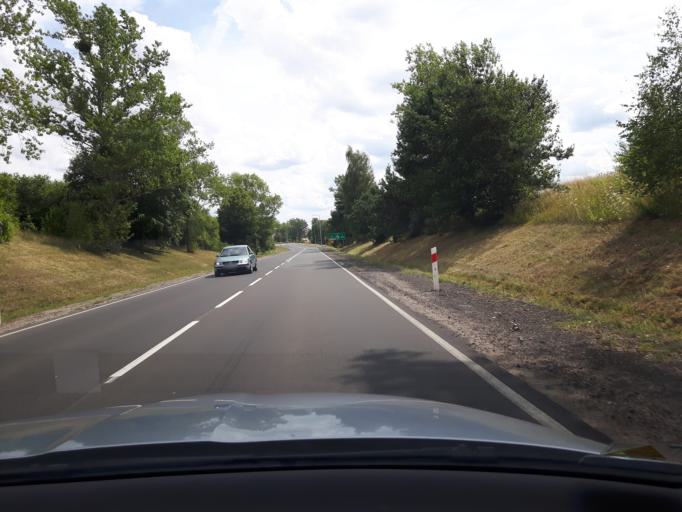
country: PL
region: Warmian-Masurian Voivodeship
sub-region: Powiat nidzicki
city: Nidzica
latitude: 53.3612
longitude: 20.3994
